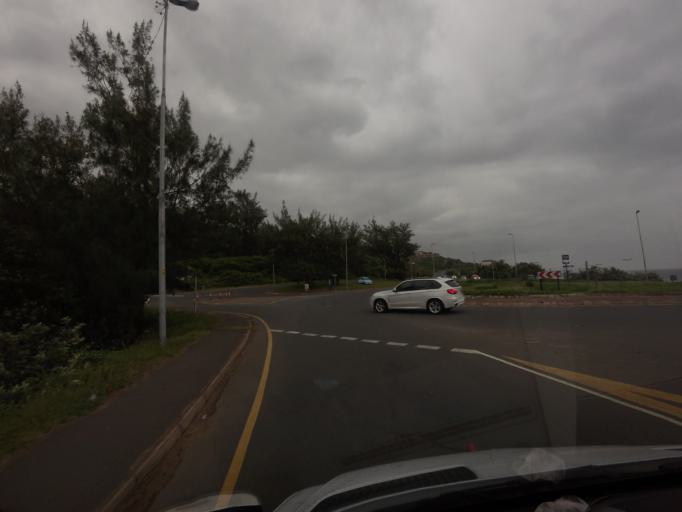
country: ZA
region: KwaZulu-Natal
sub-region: iLembe District Municipality
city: Ballitoville
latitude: -29.5929
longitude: 31.1692
